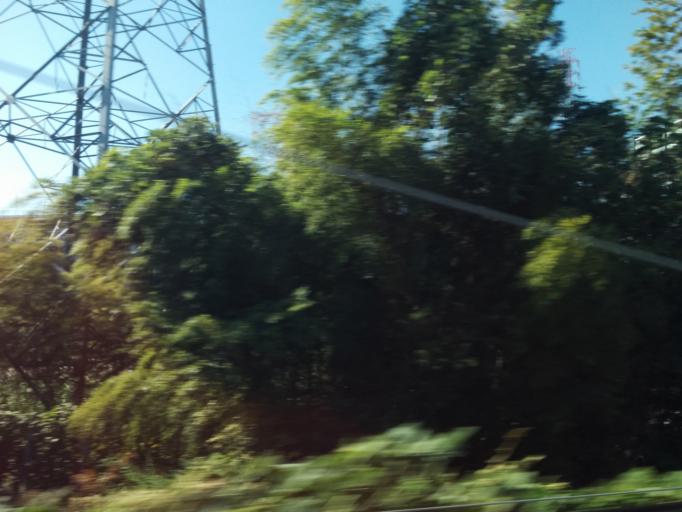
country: JP
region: Aichi
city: Obu
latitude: 35.0531
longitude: 136.9504
